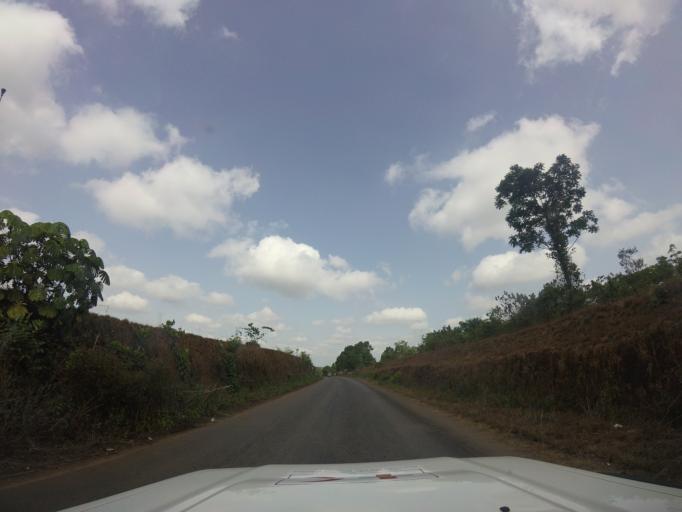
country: LR
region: Bomi
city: Tubmanburg
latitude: 6.7012
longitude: -10.9157
